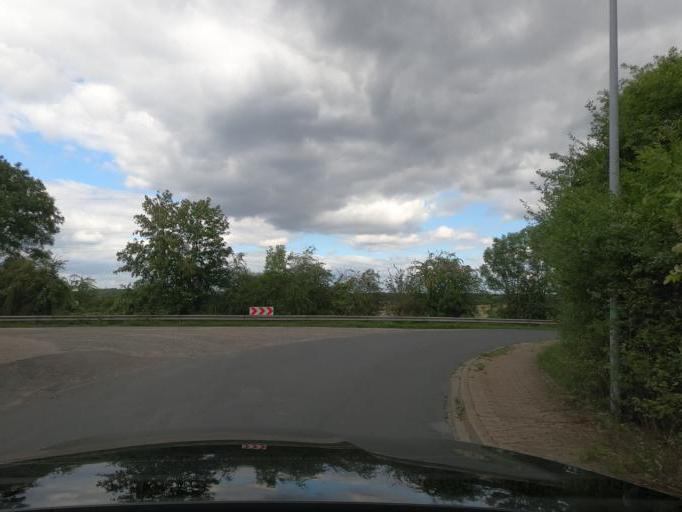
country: DE
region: Lower Saxony
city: Lehrte
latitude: 52.3770
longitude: 9.9058
